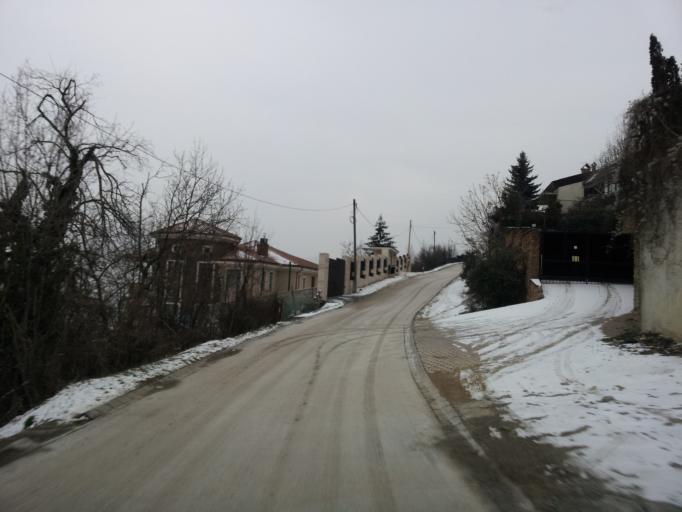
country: HU
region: Budapest
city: Budapest XII. keruelet
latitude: 47.4916
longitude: 18.9905
